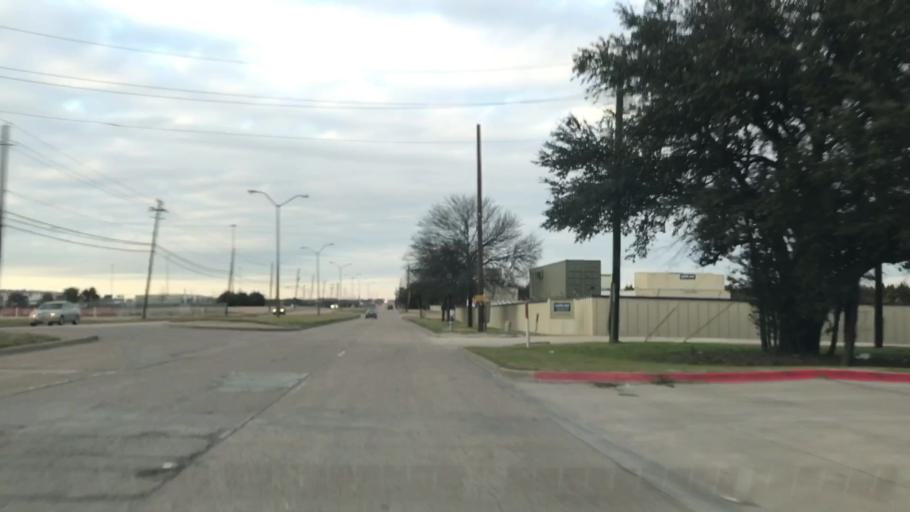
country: US
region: Texas
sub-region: Dallas County
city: Cockrell Hill
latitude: 32.6992
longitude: -96.9086
